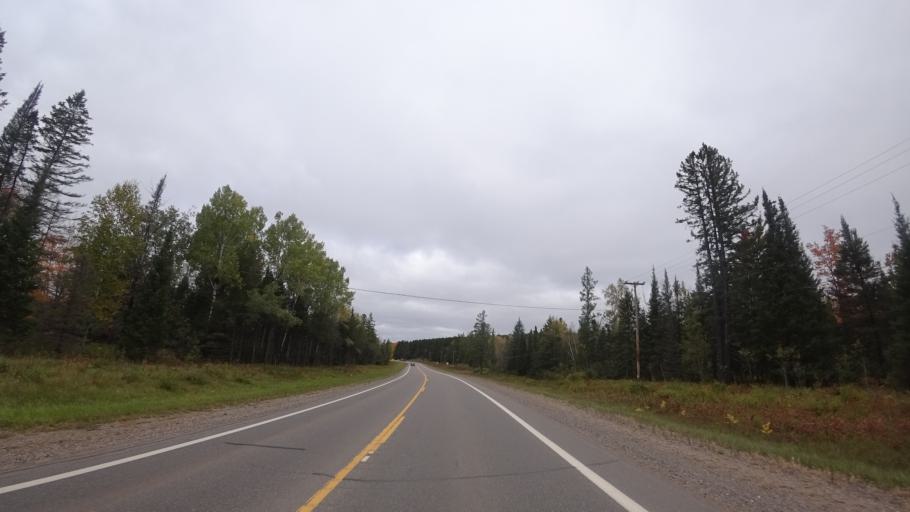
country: US
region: Wisconsin
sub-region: Florence County
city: Florence
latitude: 46.1097
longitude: -88.0763
